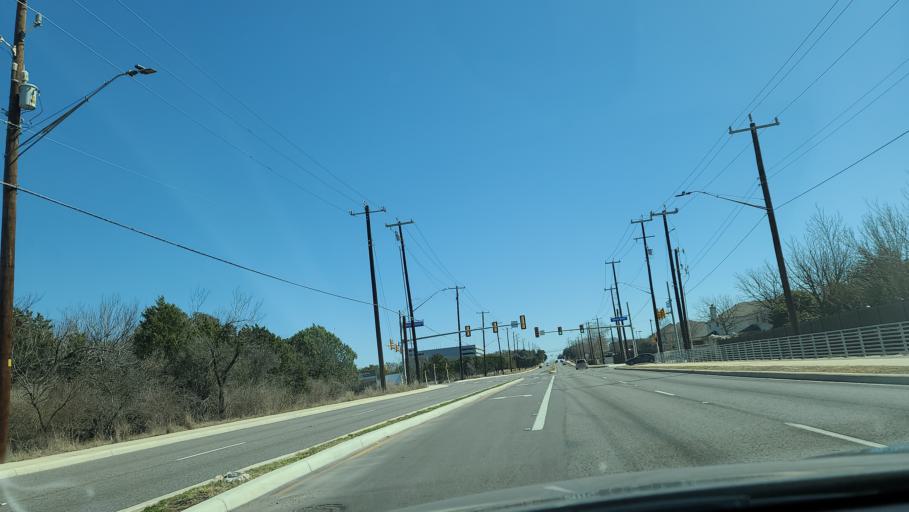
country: US
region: Texas
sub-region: Bexar County
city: Shavano Park
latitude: 29.5724
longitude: -98.6025
